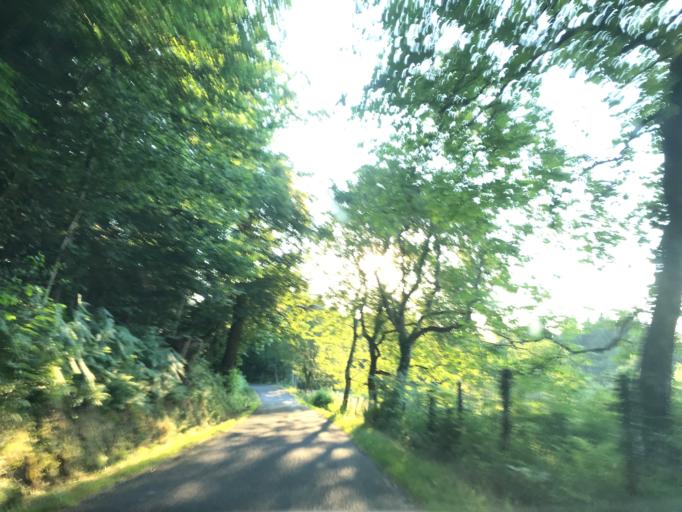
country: FR
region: Auvergne
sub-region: Departement du Puy-de-Dome
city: Courpiere
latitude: 45.7560
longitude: 3.6368
